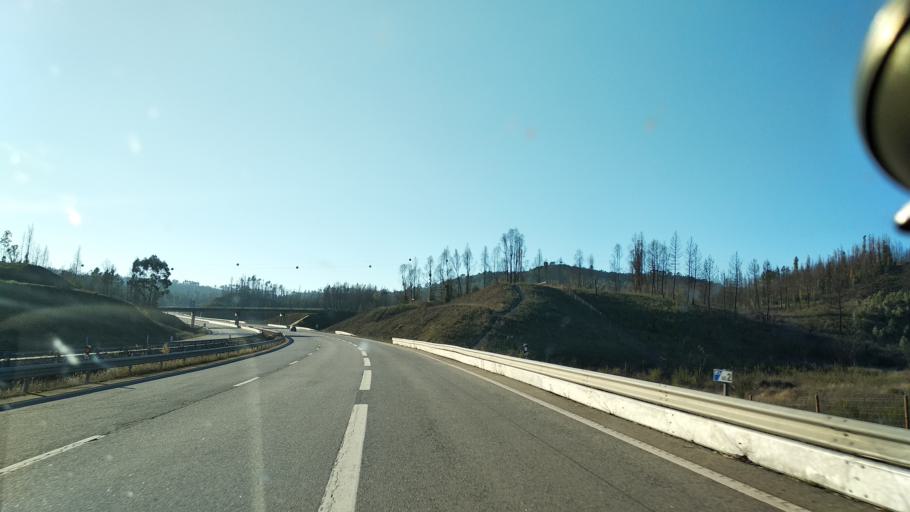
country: PT
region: Santarem
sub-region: Macao
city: Macao
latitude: 39.5220
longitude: -7.9833
